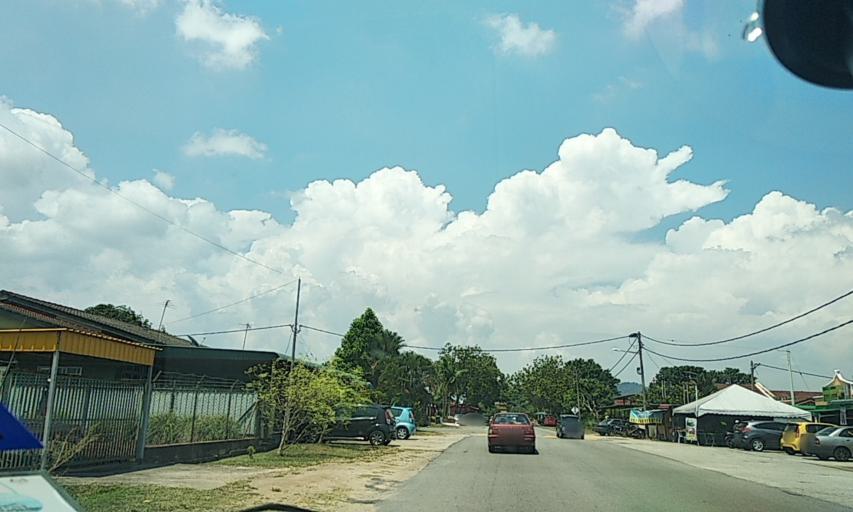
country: MY
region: Kedah
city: Sungai Petani
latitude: 5.6357
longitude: 100.4712
